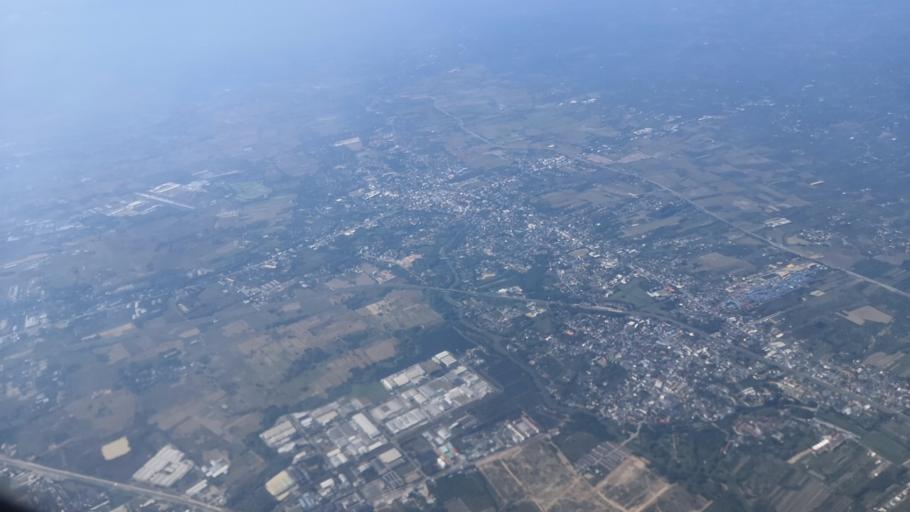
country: TH
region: Lamphun
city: Lamphun
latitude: 18.6067
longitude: 99.0563
